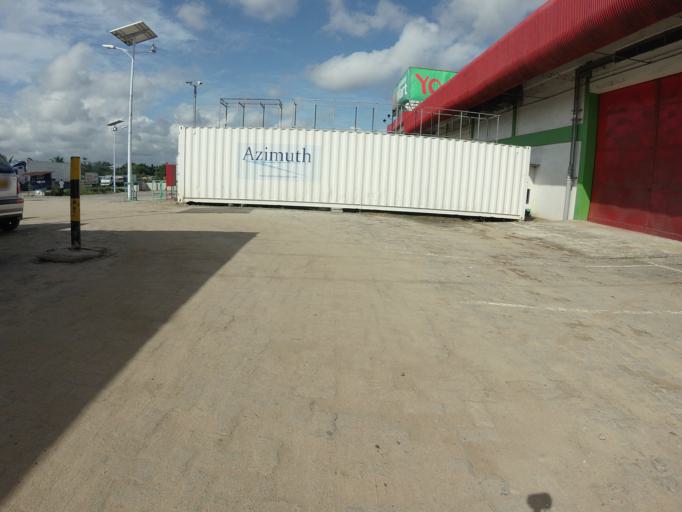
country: GH
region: Central
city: Kasoa
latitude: 5.5272
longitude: -0.4541
